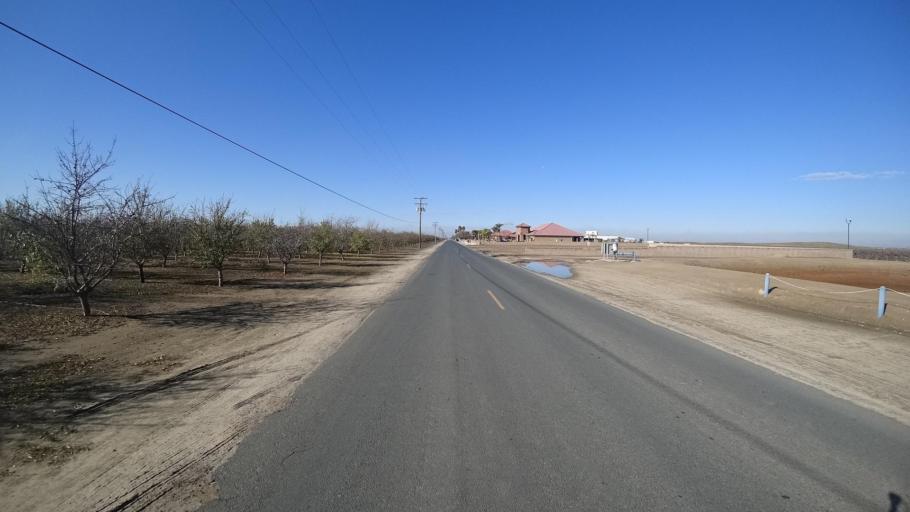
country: US
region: California
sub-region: Kern County
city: Delano
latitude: 35.7323
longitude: -119.2433
